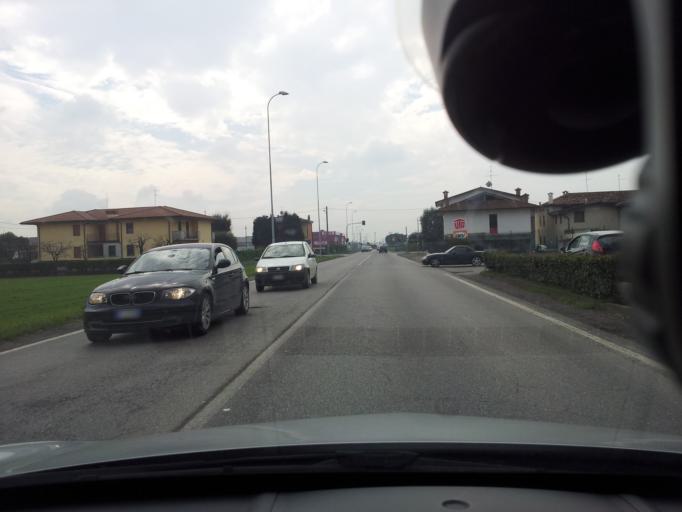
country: IT
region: Lombardy
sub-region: Provincia di Bergamo
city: Bolgare
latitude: 45.6325
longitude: 9.8079
